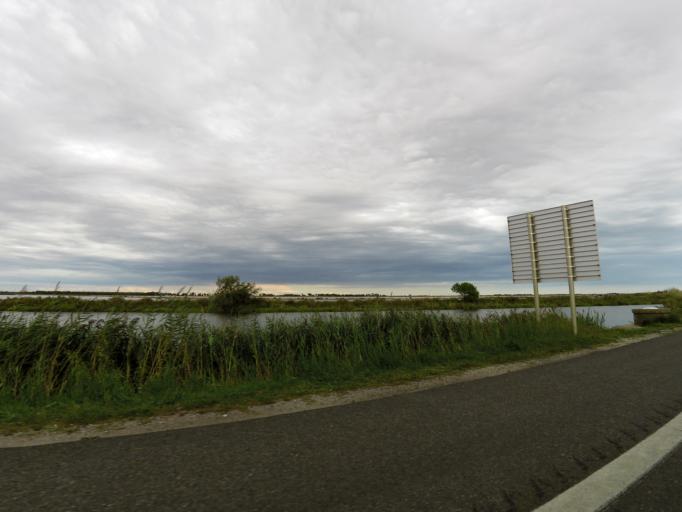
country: FR
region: Languedoc-Roussillon
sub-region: Departement du Gard
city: Le Grau-du-Roi
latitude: 43.5373
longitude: 4.1453
